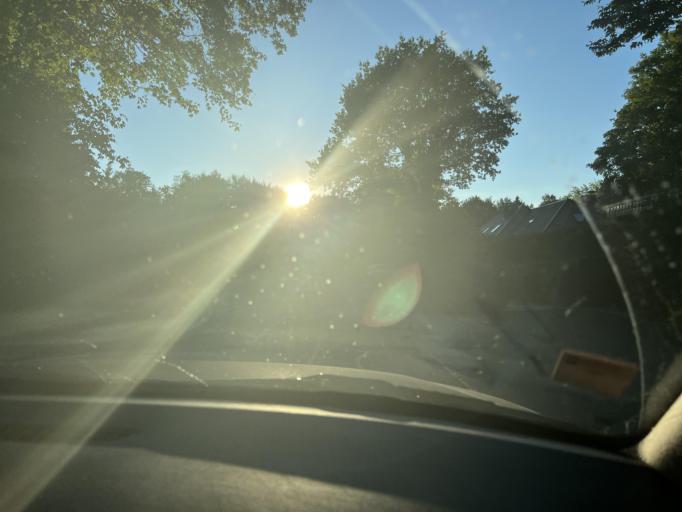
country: DE
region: Schleswig-Holstein
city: Weddingstedt
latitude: 54.2237
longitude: 9.0947
